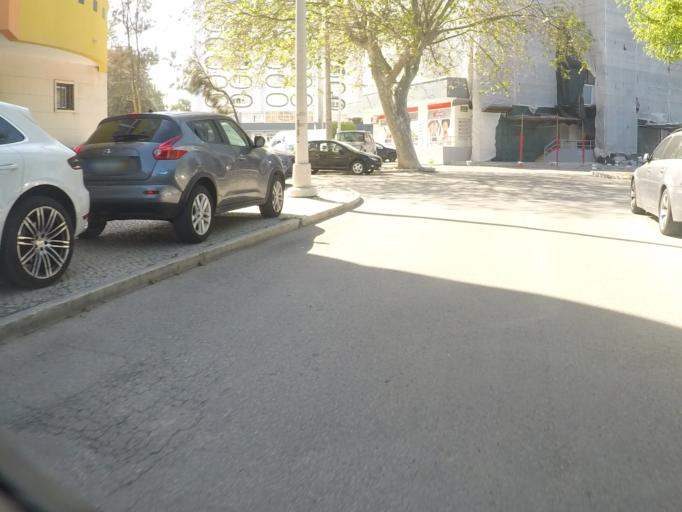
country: PT
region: Setubal
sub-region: Almada
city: Costa de Caparica
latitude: 38.6404
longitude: -9.2297
